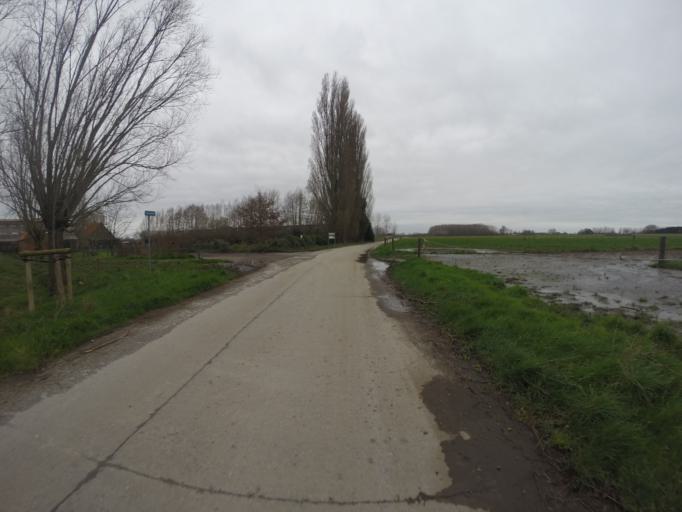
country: BE
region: Flanders
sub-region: Provincie Oost-Vlaanderen
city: Aalter
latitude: 51.1227
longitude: 3.4557
